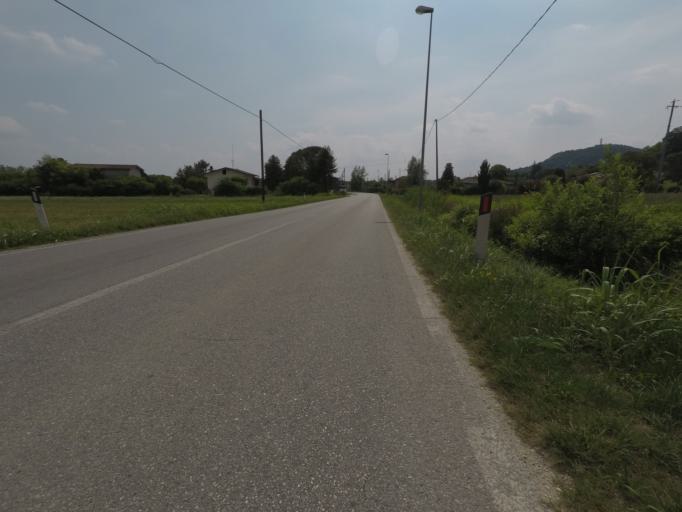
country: IT
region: Friuli Venezia Giulia
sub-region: Provincia di Pordenone
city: Caneva
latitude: 45.9913
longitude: 12.4797
